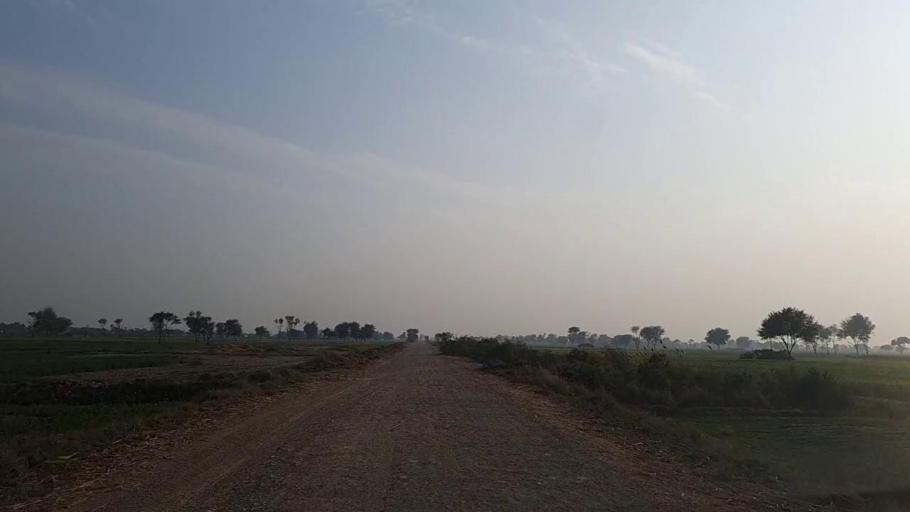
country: PK
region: Sindh
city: Jam Sahib
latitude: 26.3170
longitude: 68.5336
